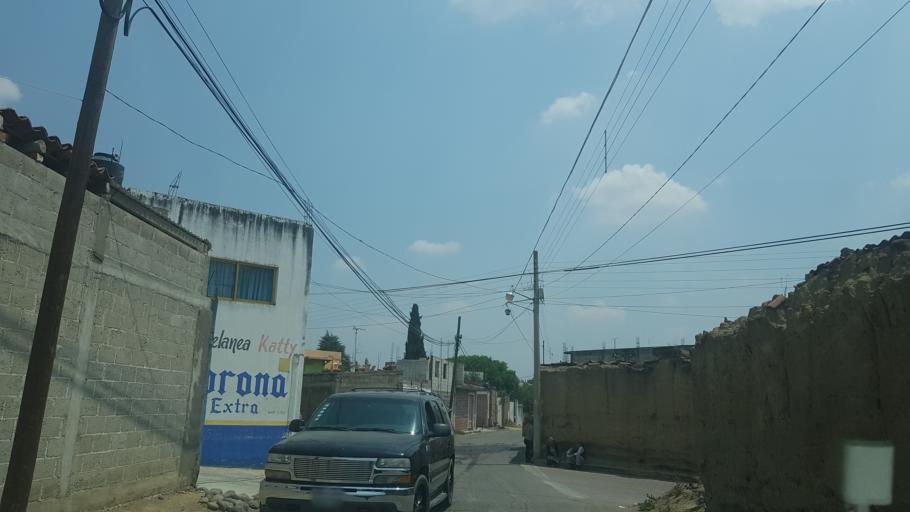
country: MX
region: Puebla
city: San Andres Calpan
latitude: 19.1049
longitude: -98.4676
